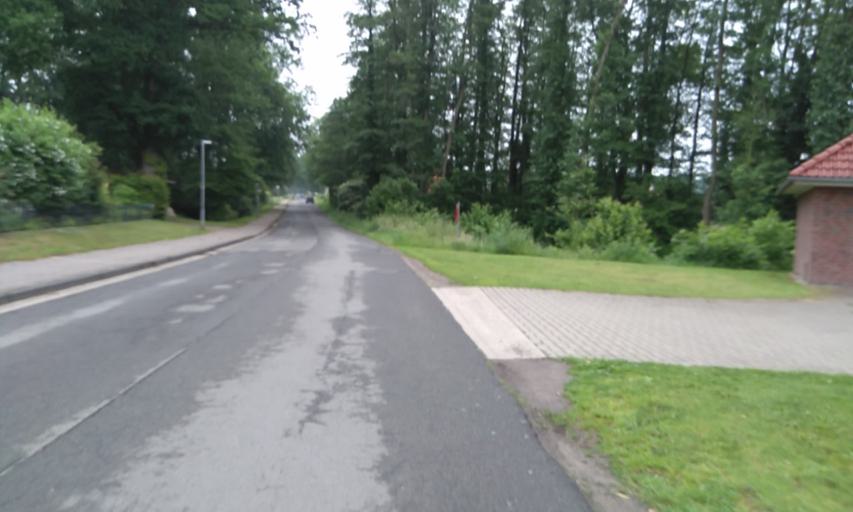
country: DE
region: Lower Saxony
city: Deinste
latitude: 53.5491
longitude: 9.4612
